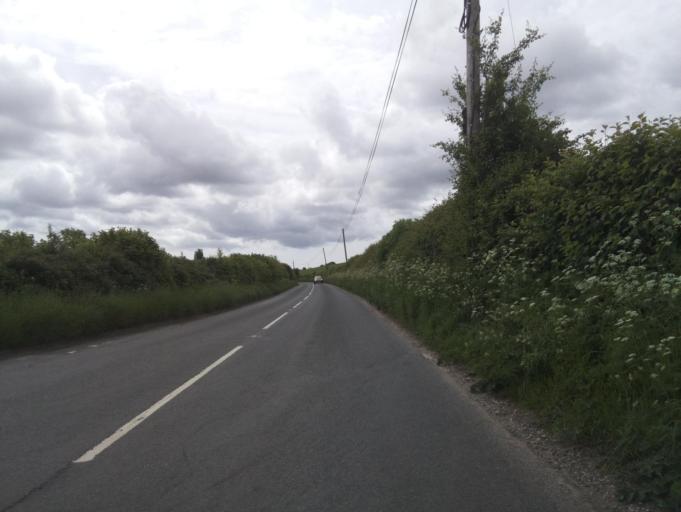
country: GB
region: England
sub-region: Dorset
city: Dorchester
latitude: 50.7464
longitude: -2.4616
